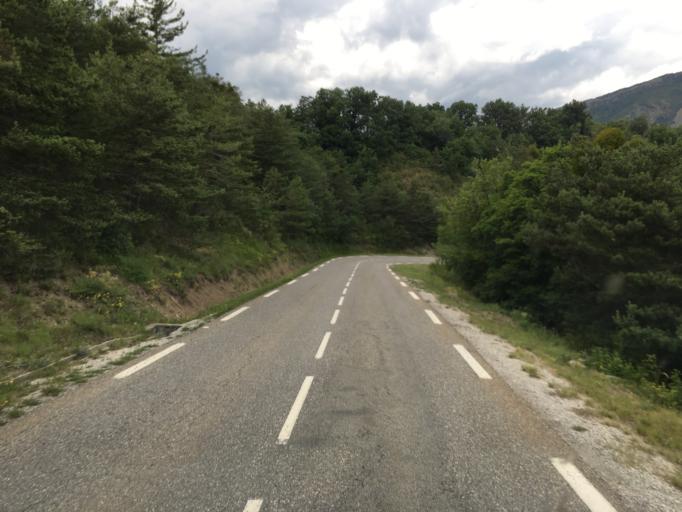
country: FR
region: Provence-Alpes-Cote d'Azur
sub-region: Departement des Hautes-Alpes
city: Veynes
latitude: 44.5319
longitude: 5.7999
